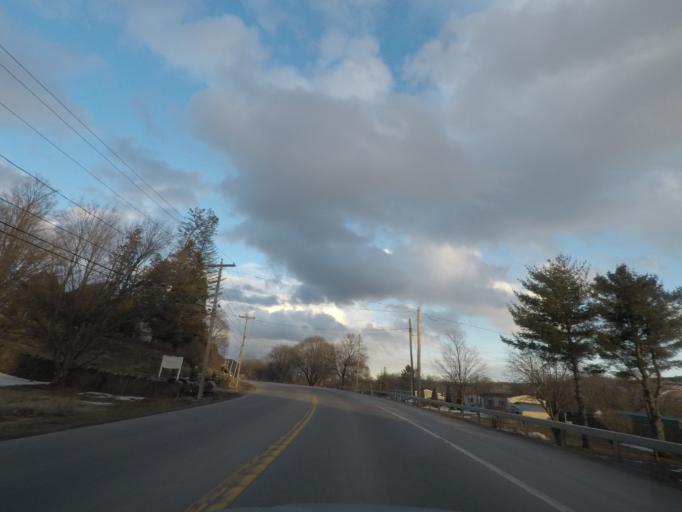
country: US
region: New York
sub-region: Montgomery County
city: Saint Johnsville
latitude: 42.9985
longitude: -74.6984
